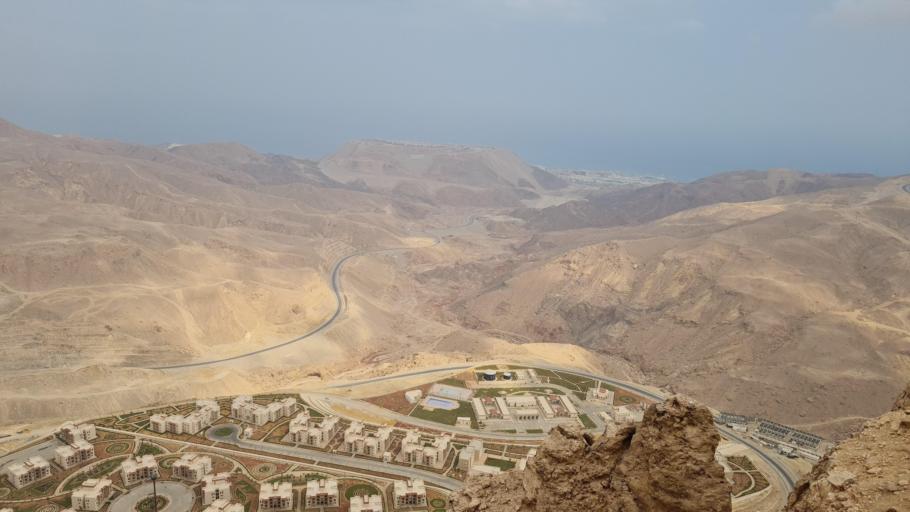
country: EG
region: As Suways
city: Ain Sukhna
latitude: 29.4474
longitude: 32.4105
